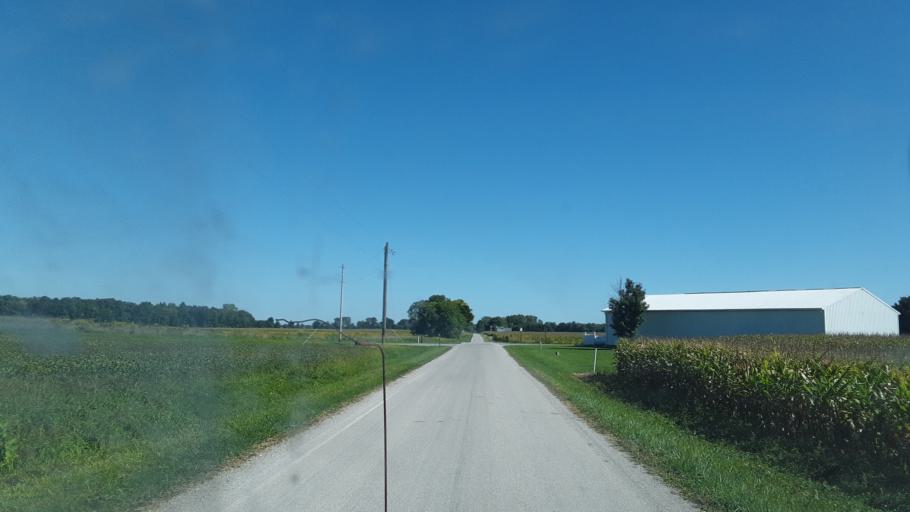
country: US
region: Ohio
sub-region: Wyandot County
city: Upper Sandusky
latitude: 40.9335
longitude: -83.2420
